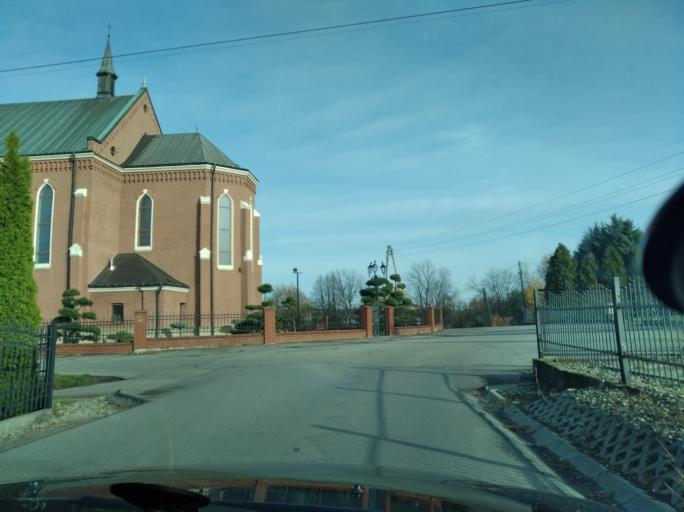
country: PL
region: Subcarpathian Voivodeship
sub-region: Powiat rzeszowski
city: Krasne
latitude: 50.0275
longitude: 22.1058
